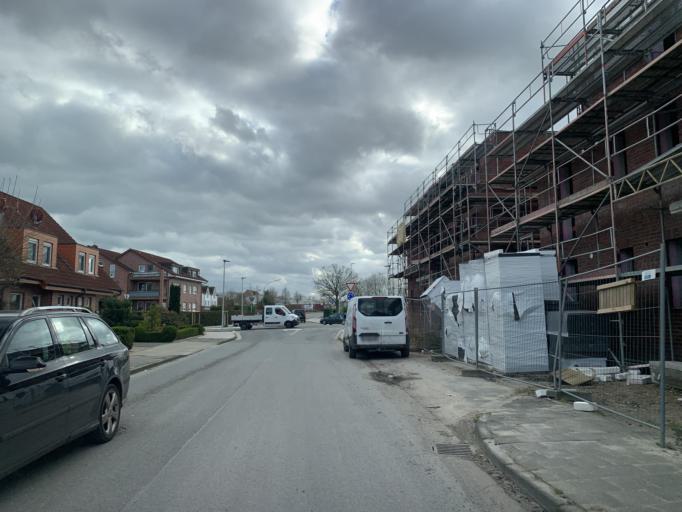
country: DE
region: North Rhine-Westphalia
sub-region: Regierungsbezirk Munster
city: Steinfurt
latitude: 52.1193
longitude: 7.4021
